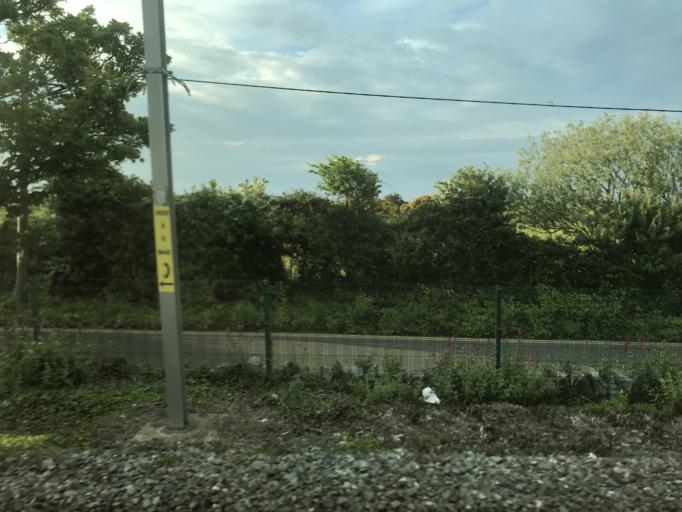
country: IE
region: Leinster
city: Sutton
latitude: 53.3919
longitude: -6.1110
